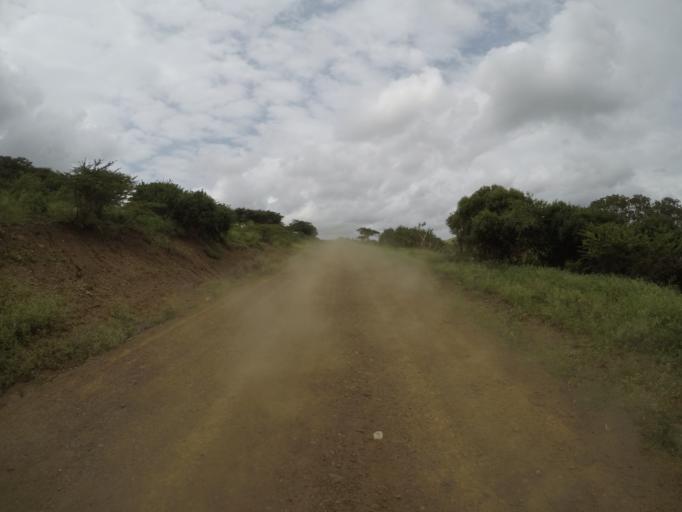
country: ZA
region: KwaZulu-Natal
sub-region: uThungulu District Municipality
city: Empangeni
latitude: -28.6060
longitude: 31.8944
